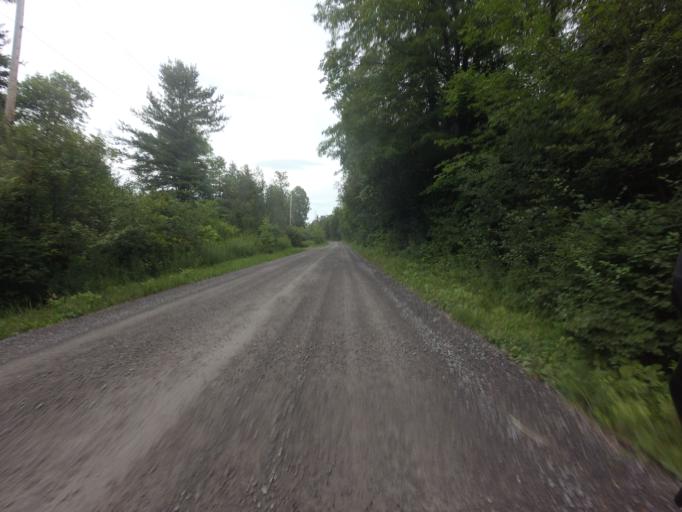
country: CA
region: Ontario
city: Carleton Place
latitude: 45.1492
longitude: -76.2141
